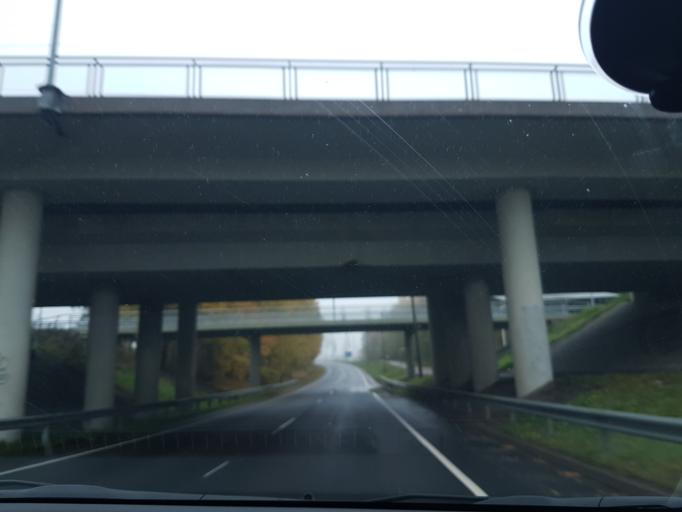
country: FI
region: Uusimaa
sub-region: Helsinki
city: Jaervenpaeae
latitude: 60.4557
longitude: 25.1014
